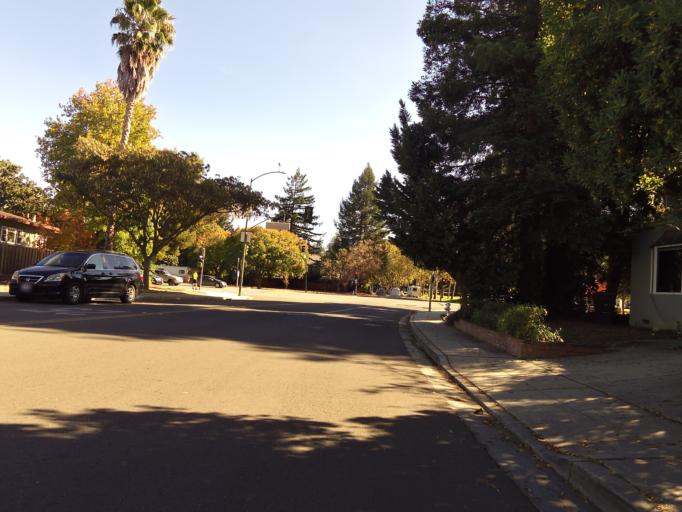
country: US
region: California
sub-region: Santa Clara County
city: Mountain View
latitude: 37.3907
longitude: -122.0872
